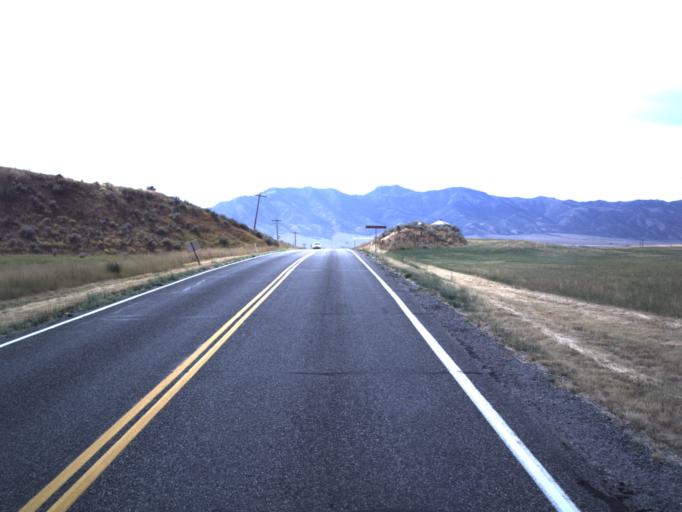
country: US
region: Utah
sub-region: Cache County
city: Lewiston
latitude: 41.9175
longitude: -111.9739
